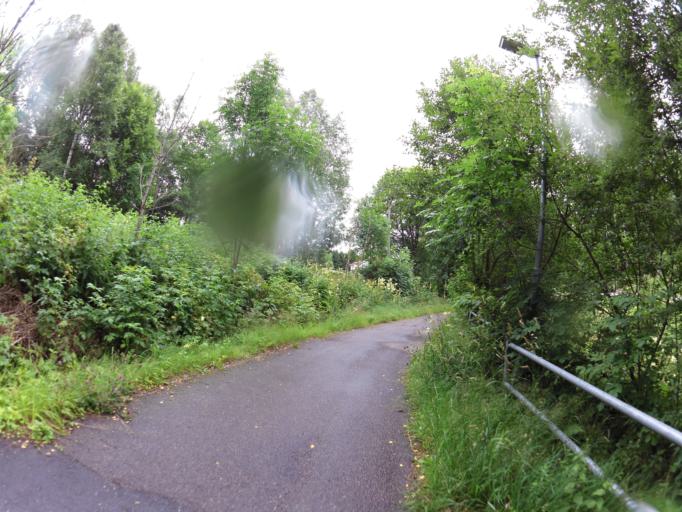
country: NO
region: Ostfold
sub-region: Moss
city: Moss
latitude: 59.4681
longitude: 10.6900
